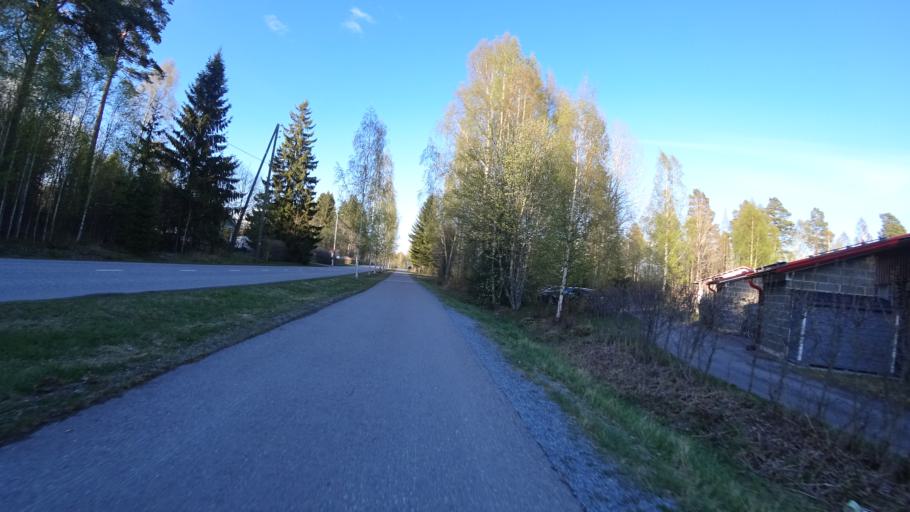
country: FI
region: Pirkanmaa
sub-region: Tampere
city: Nokia
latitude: 61.4916
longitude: 23.5545
